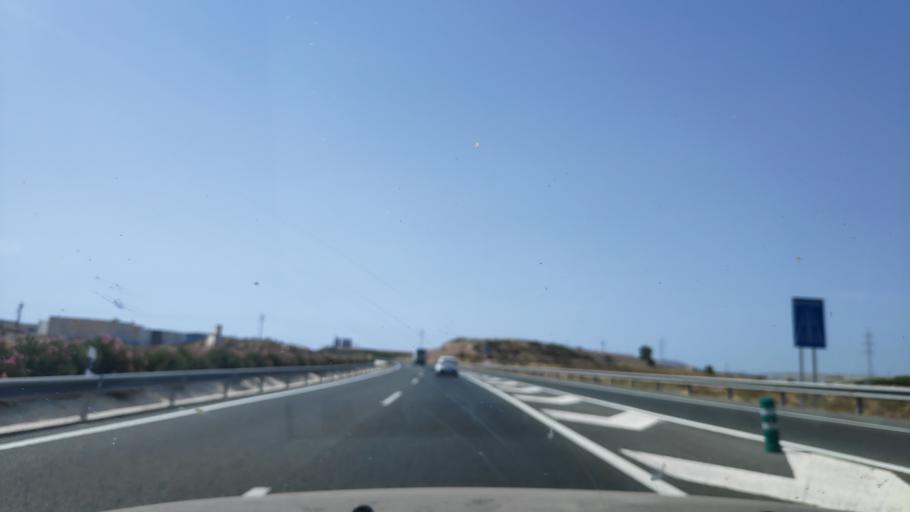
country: ES
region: Murcia
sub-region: Murcia
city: Blanca
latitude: 38.1944
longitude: -1.3326
